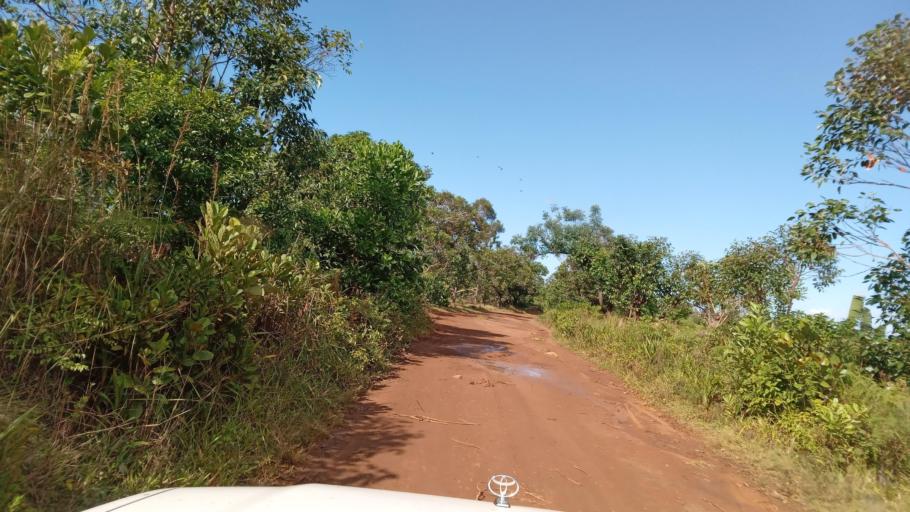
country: MG
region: Atsimo-Atsinanana
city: Vohipaho
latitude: -23.7240
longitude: 47.5662
